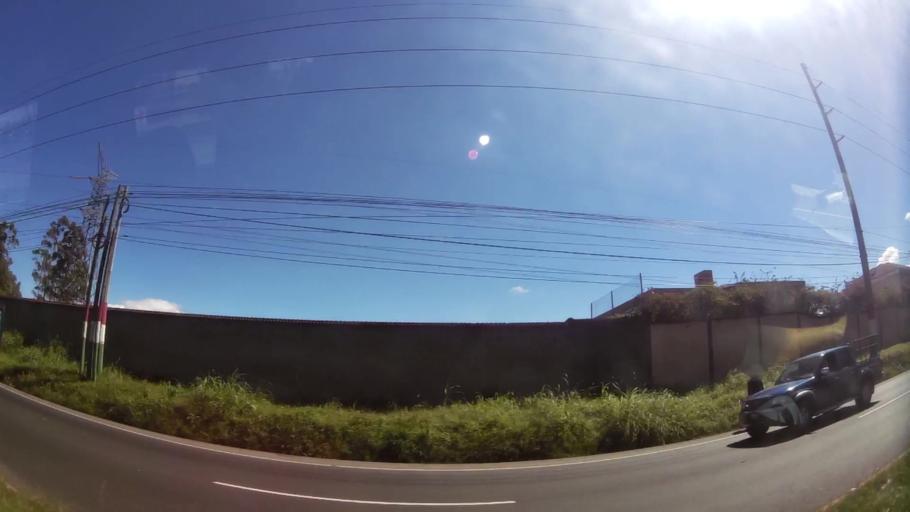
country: GT
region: Guatemala
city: Santa Catarina Pinula
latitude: 14.5234
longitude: -90.4690
